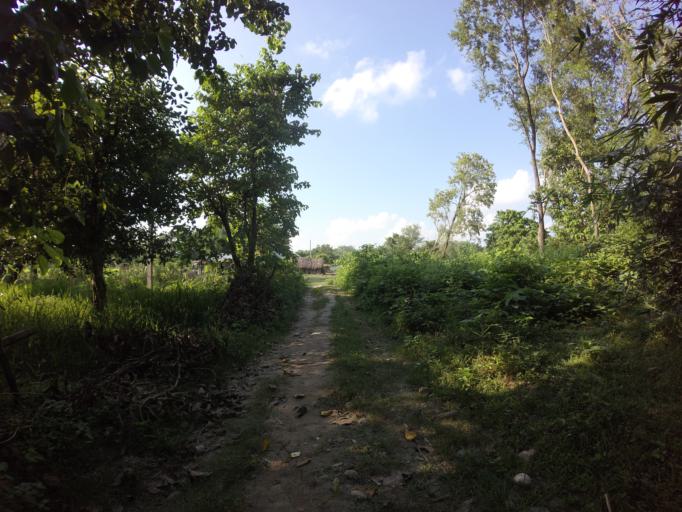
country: NP
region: Far Western
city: Tikapur
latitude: 28.4441
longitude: 81.0778
